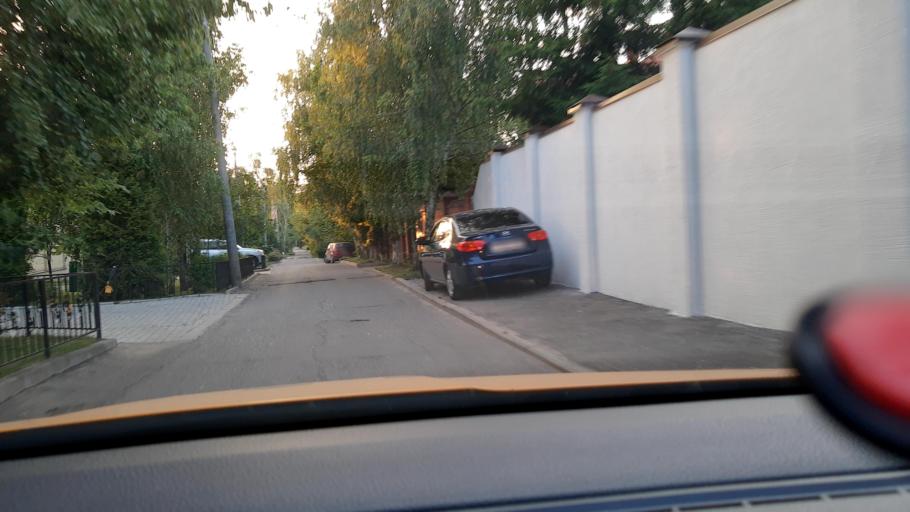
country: RU
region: Moskovskaya
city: Barvikha
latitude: 55.7227
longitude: 37.3000
